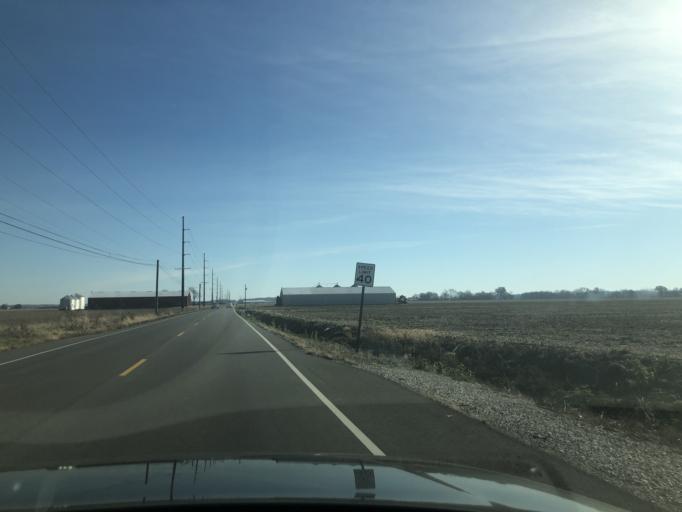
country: US
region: Indiana
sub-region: Vanderburgh County
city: Melody Hill
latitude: 37.9912
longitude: -87.4587
